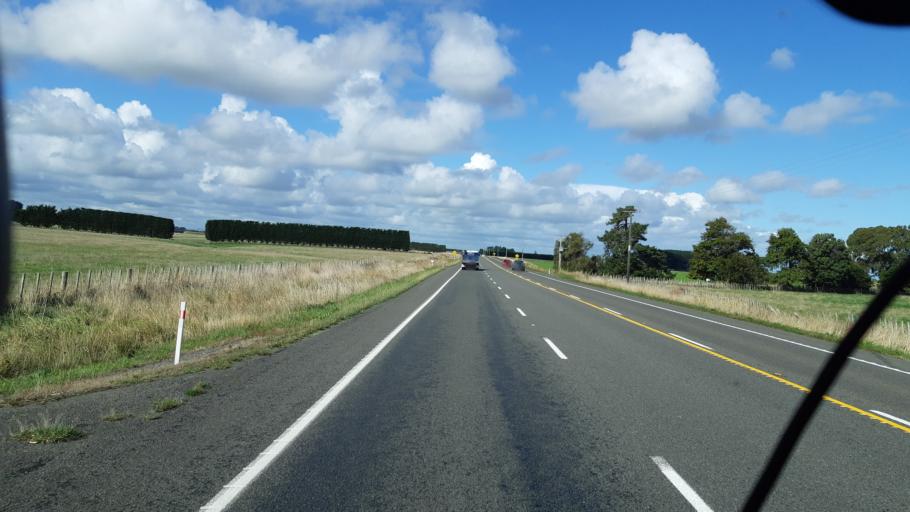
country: NZ
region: Manawatu-Wanganui
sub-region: Wanganui District
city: Wanganui
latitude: -39.9838
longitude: 175.1518
